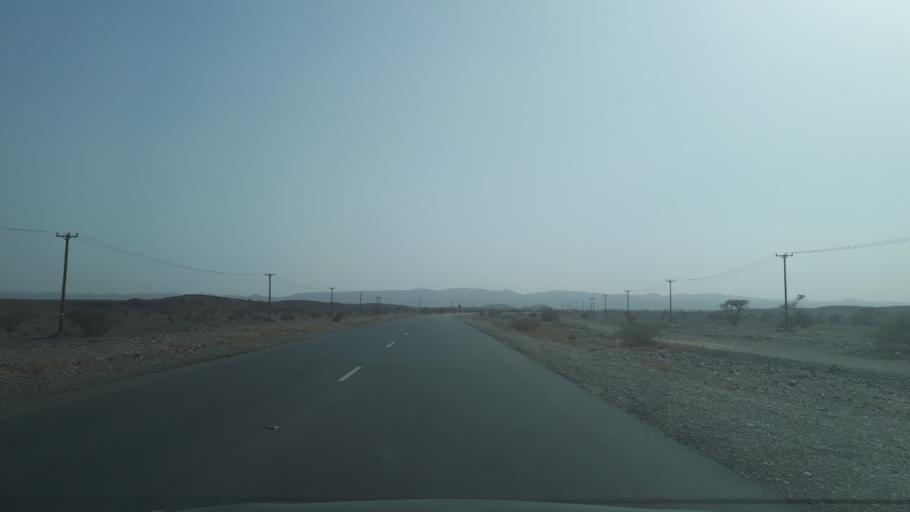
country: OM
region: Az Zahirah
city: `Ibri
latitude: 23.1012
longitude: 56.8623
